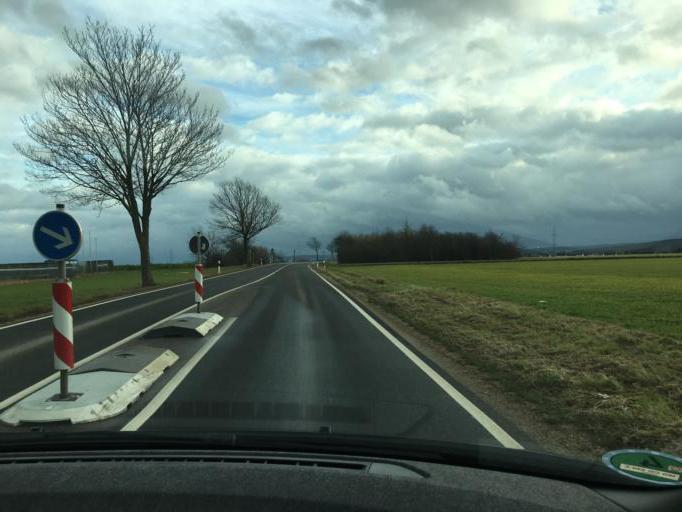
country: DE
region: North Rhine-Westphalia
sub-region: Regierungsbezirk Koln
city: Euskirchen
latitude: 50.6625
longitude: 6.7394
